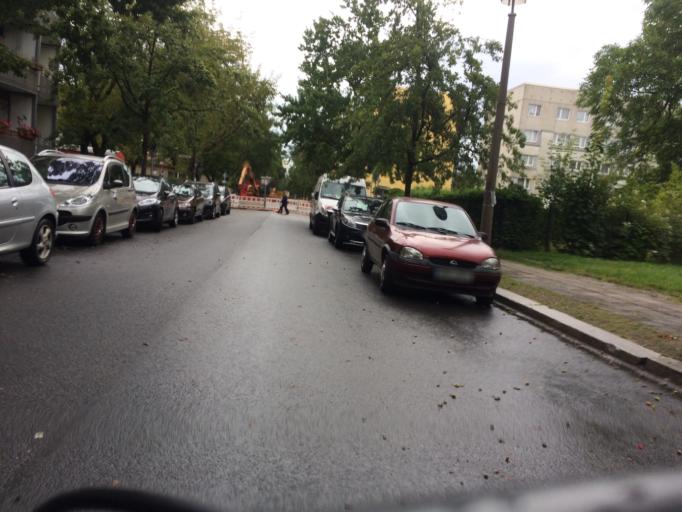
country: DE
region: Berlin
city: Buchholz
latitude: 52.5850
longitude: 13.4242
